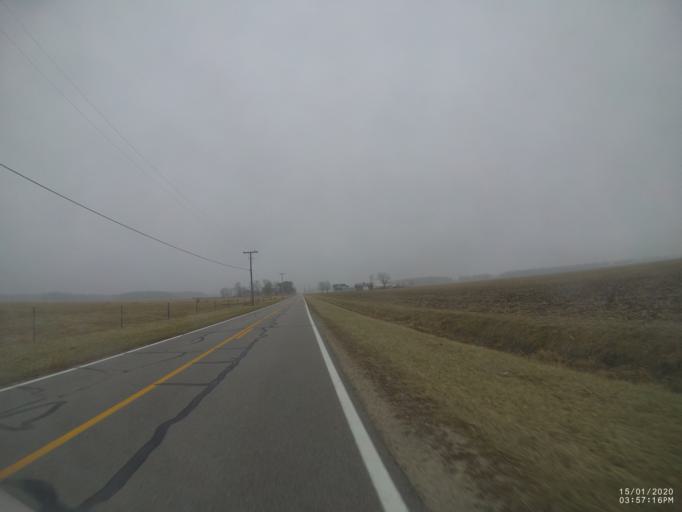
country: US
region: Ohio
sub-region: Sandusky County
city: Woodville
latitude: 41.4138
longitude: -83.3856
